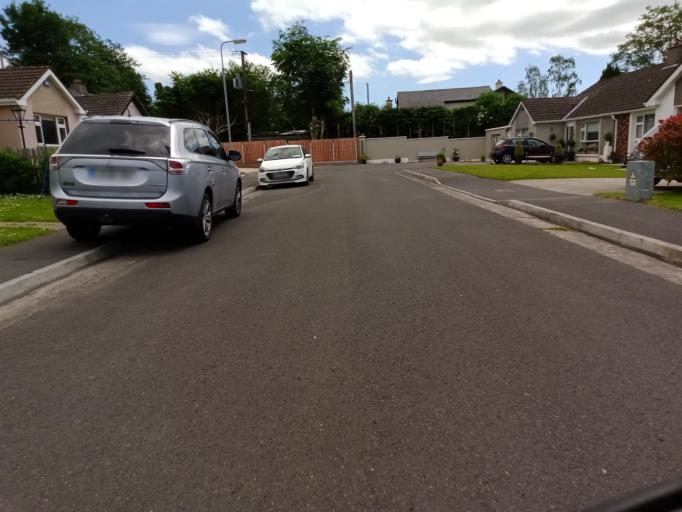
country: IE
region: Leinster
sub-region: Kilkenny
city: Kilkenny
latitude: 52.6530
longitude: -7.2378
